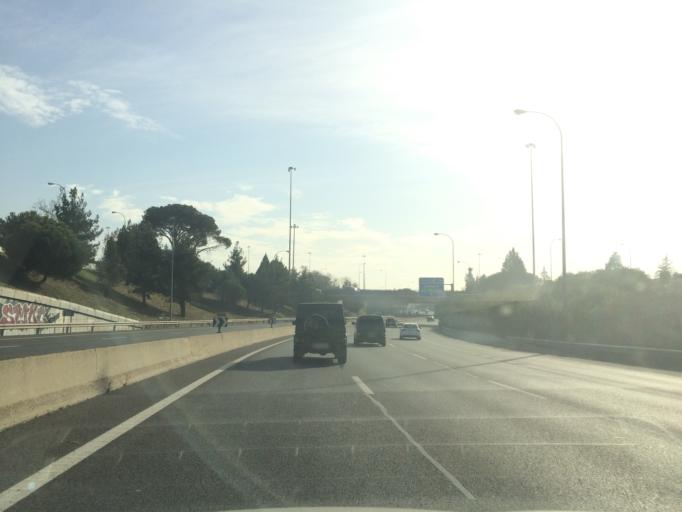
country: ES
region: Madrid
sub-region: Provincia de Madrid
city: Moncloa-Aravaca
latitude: 40.4560
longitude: -3.7437
